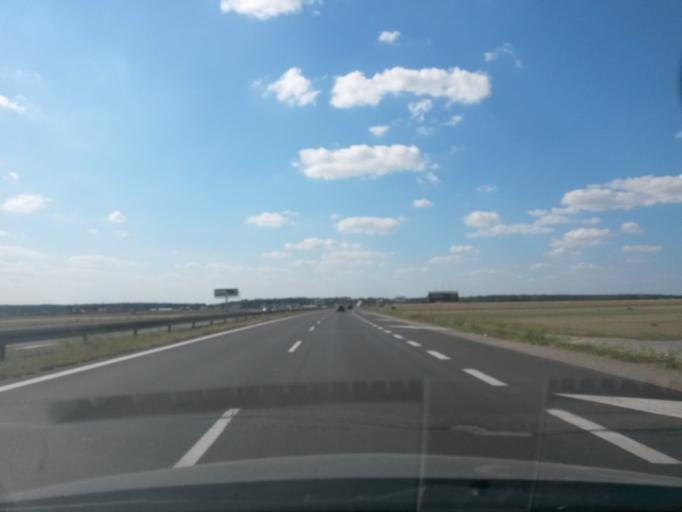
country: PL
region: Masovian Voivodeship
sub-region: Powiat nowodworski
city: Zakroczym
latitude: 52.4458
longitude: 20.6083
